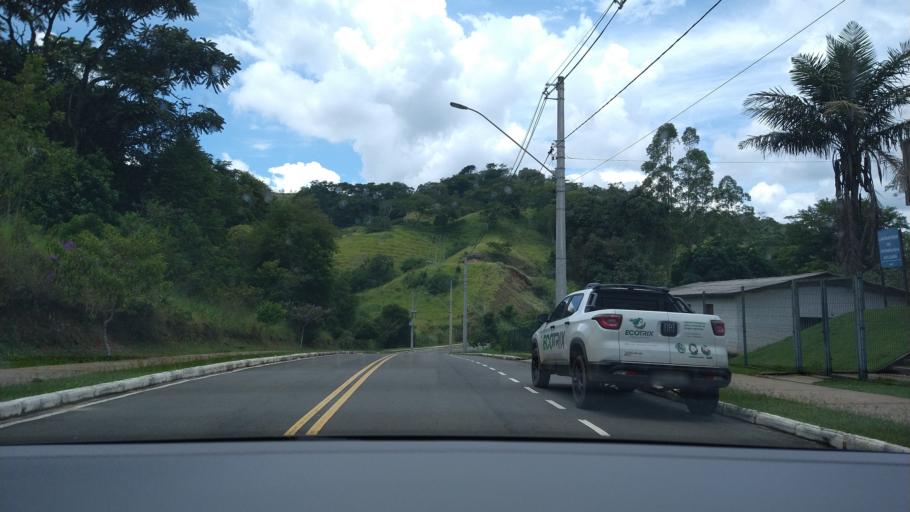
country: BR
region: Minas Gerais
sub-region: Vicosa
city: Vicosa
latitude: -20.7621
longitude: -42.8599
